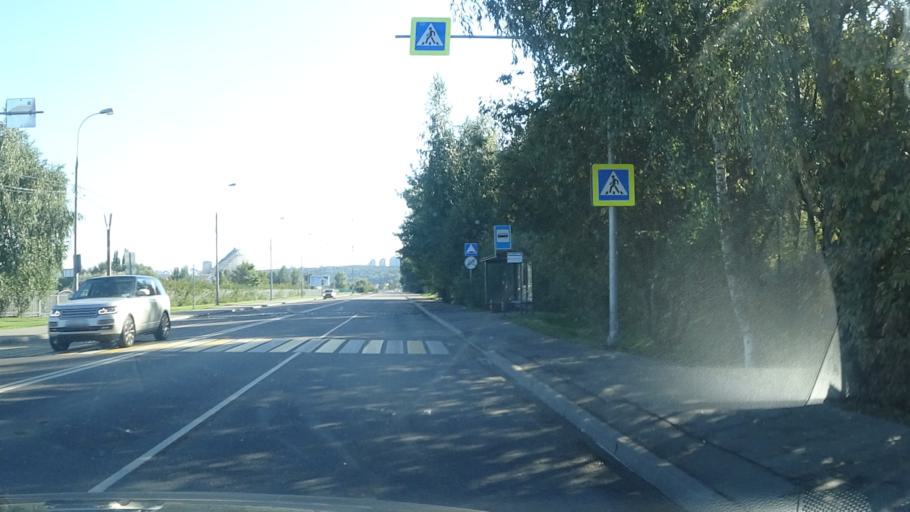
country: RU
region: Moscow
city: Shchukino
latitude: 55.7630
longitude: 37.4302
